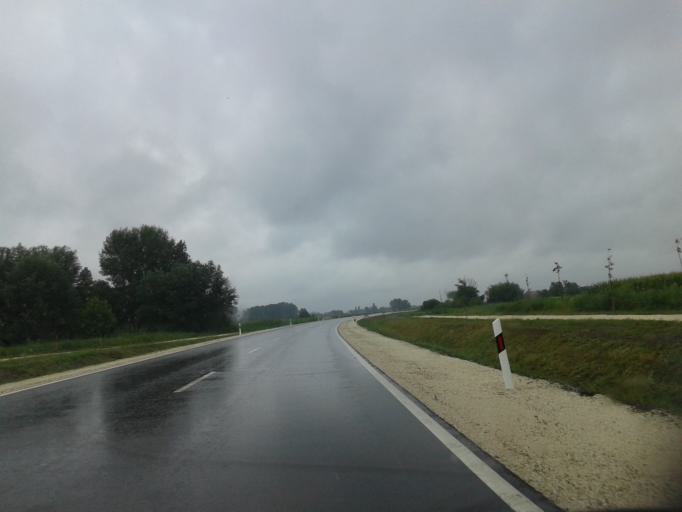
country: HU
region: Csongrad
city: Morahalom
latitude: 46.2373
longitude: 19.8797
